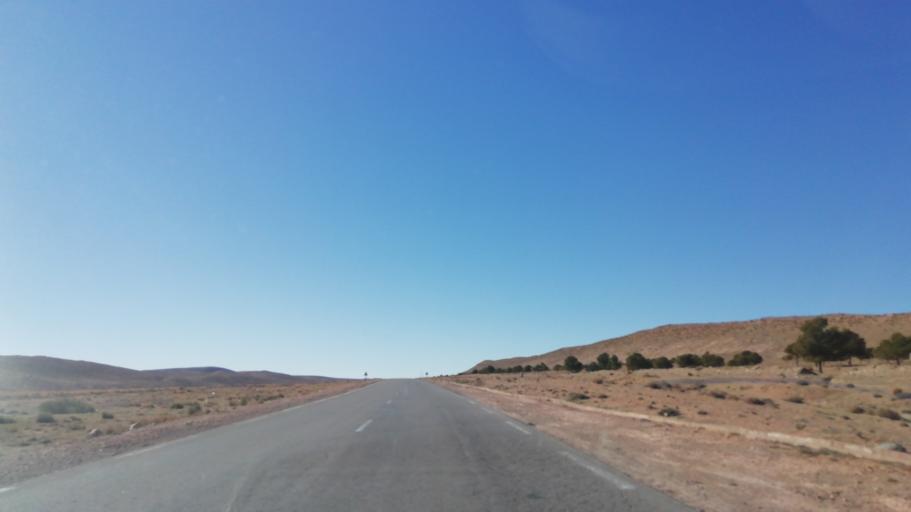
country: DZ
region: El Bayadh
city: El Bayadh
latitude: 33.6870
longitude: 1.4608
